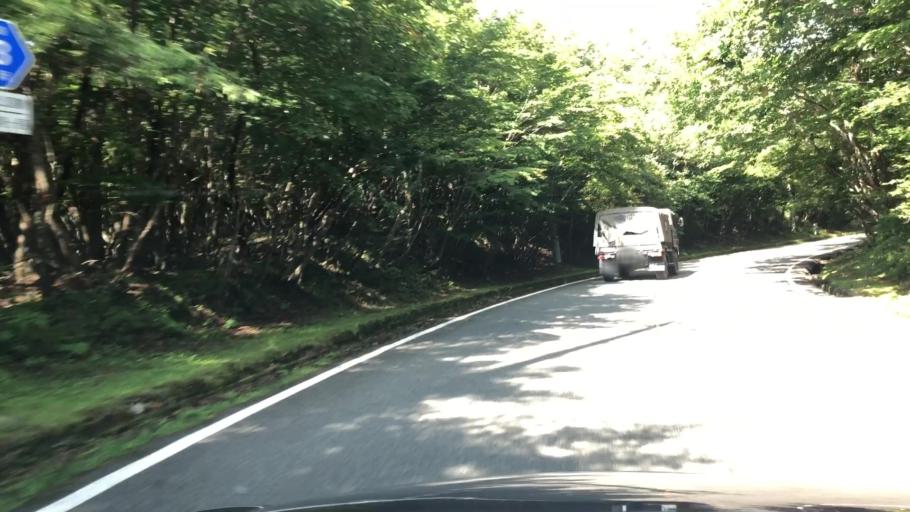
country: JP
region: Shizuoka
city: Gotemba
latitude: 35.3326
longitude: 138.8203
